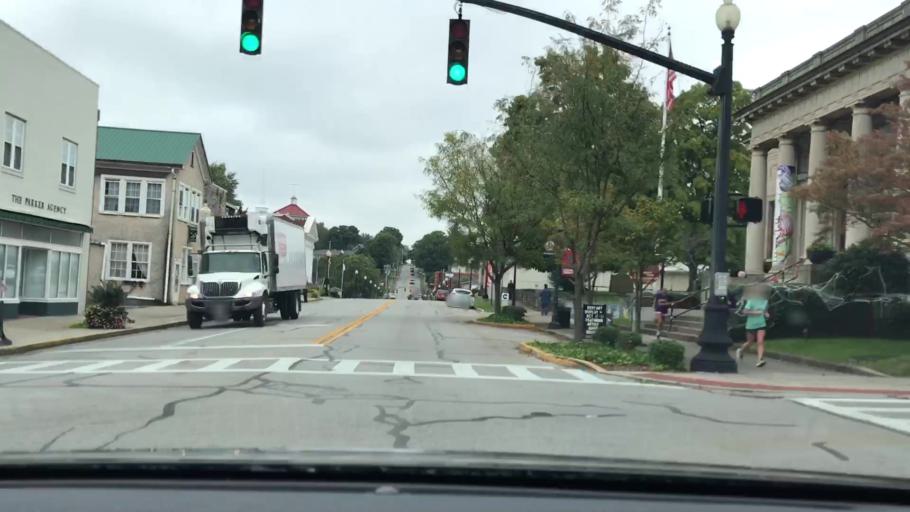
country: US
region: Kentucky
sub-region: Pulaski County
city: Somerset
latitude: 37.0927
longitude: -84.6049
